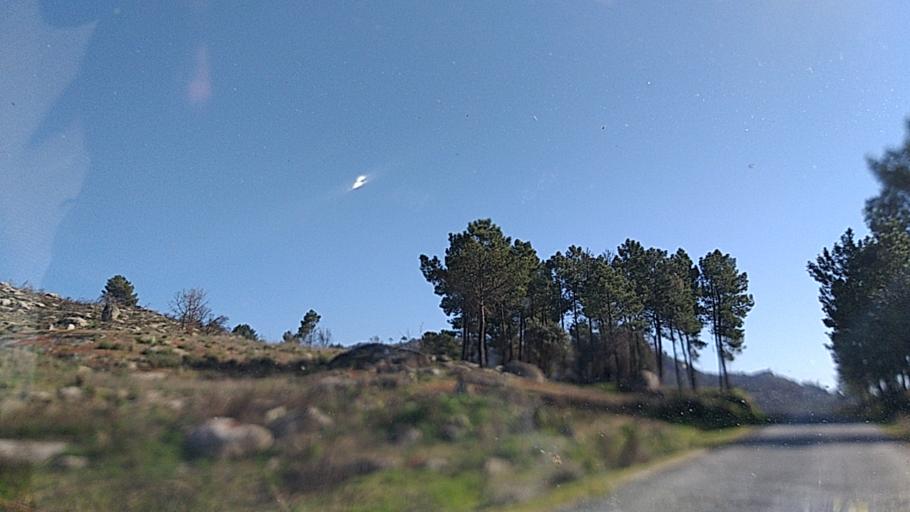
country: PT
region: Guarda
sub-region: Celorico da Beira
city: Celorico da Beira
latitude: 40.6906
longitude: -7.4265
